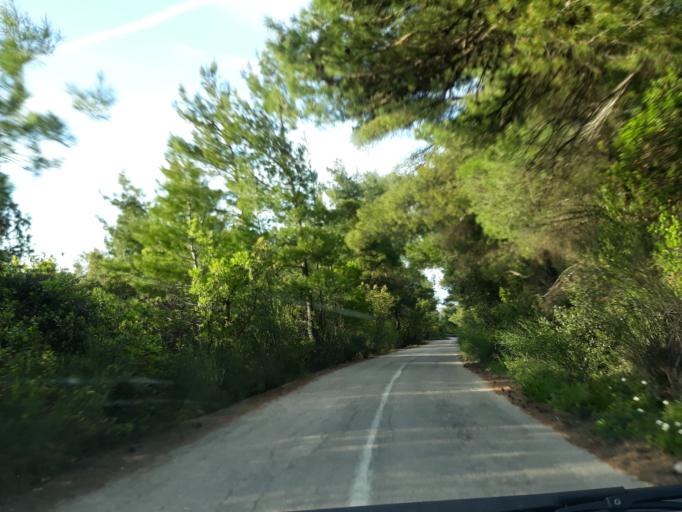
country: GR
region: Attica
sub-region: Nomarchia Anatolikis Attikis
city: Afidnes
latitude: 38.2218
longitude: 23.7837
